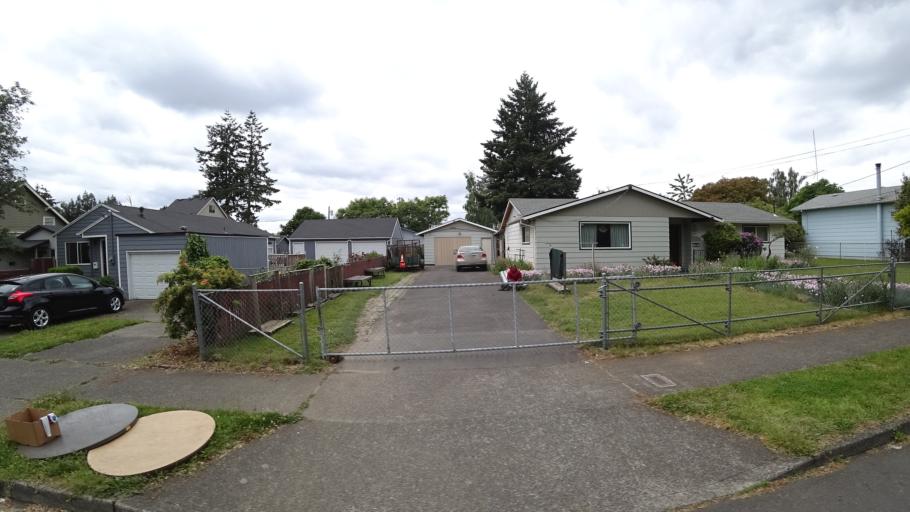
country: US
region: Oregon
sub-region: Multnomah County
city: Lents
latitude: 45.4875
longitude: -122.5724
